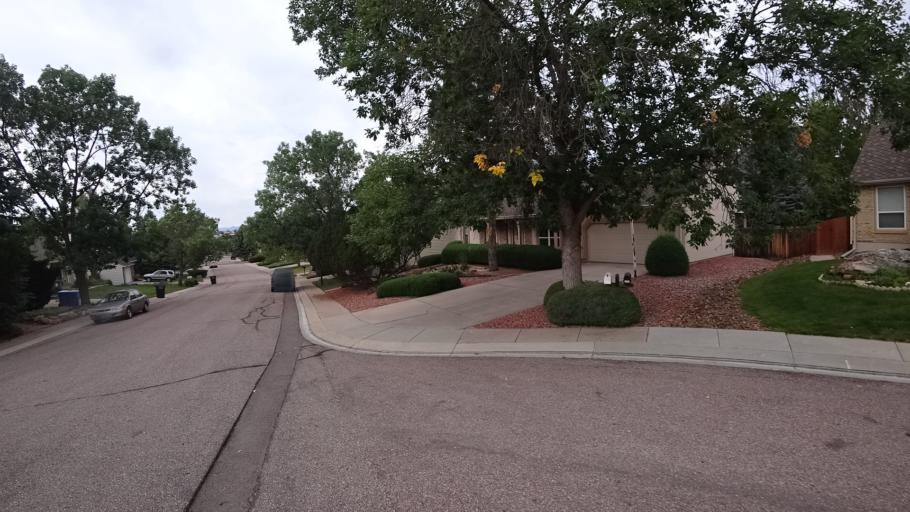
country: US
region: Colorado
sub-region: El Paso County
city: Air Force Academy
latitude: 38.9233
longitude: -104.8324
